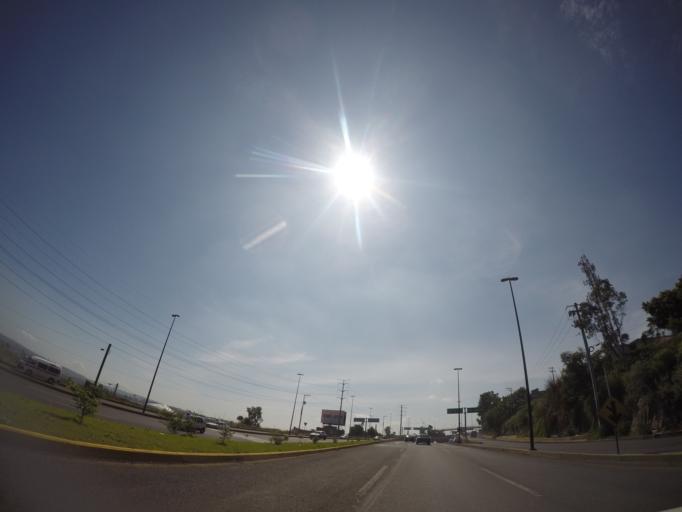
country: MX
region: Michoacan
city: Morelia
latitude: 19.7243
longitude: -101.1960
